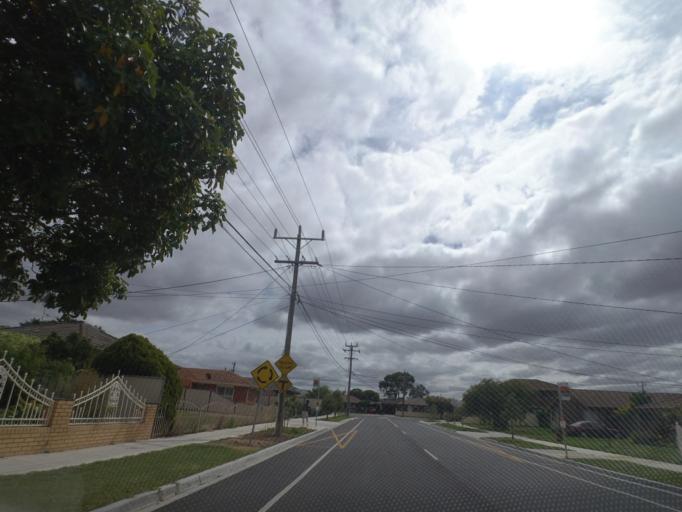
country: AU
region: Victoria
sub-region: Brimbank
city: Deer Park
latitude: -37.7516
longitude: 144.7622
